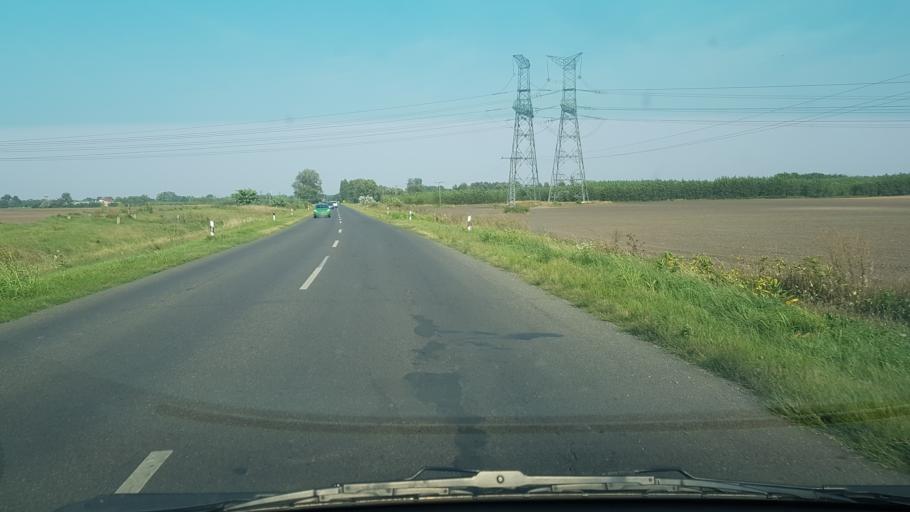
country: HU
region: Pest
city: Cegledbercel
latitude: 47.2335
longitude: 19.6530
